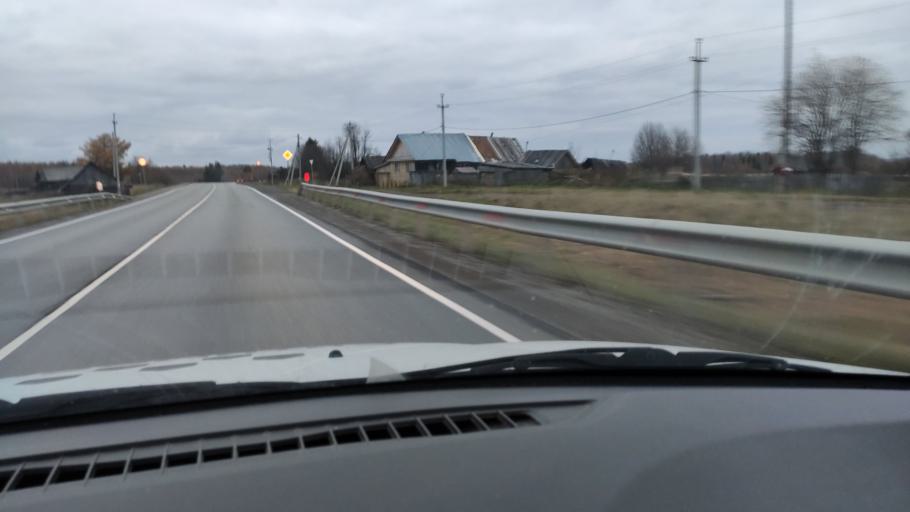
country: RU
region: Kirov
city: Kostino
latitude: 58.7965
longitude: 52.8905
